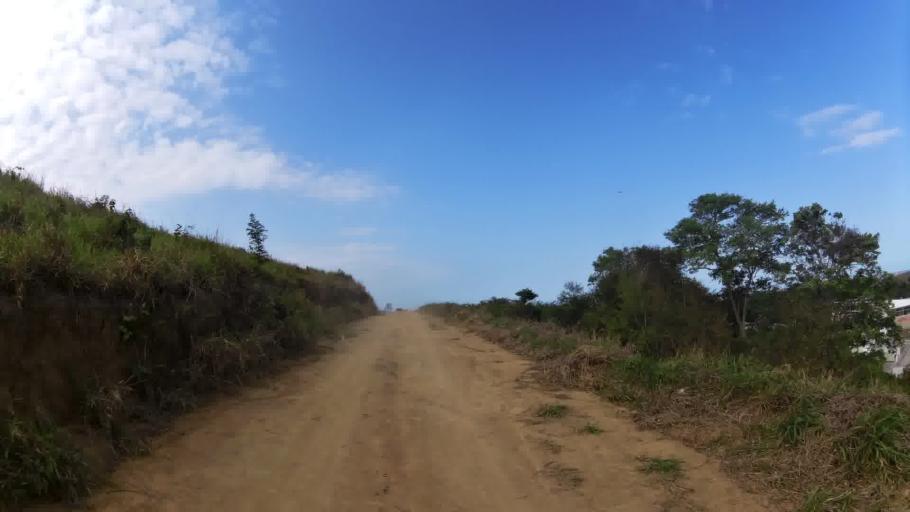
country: BR
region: Espirito Santo
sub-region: Itapemirim
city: Itapemirim
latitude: -21.0076
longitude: -40.8315
